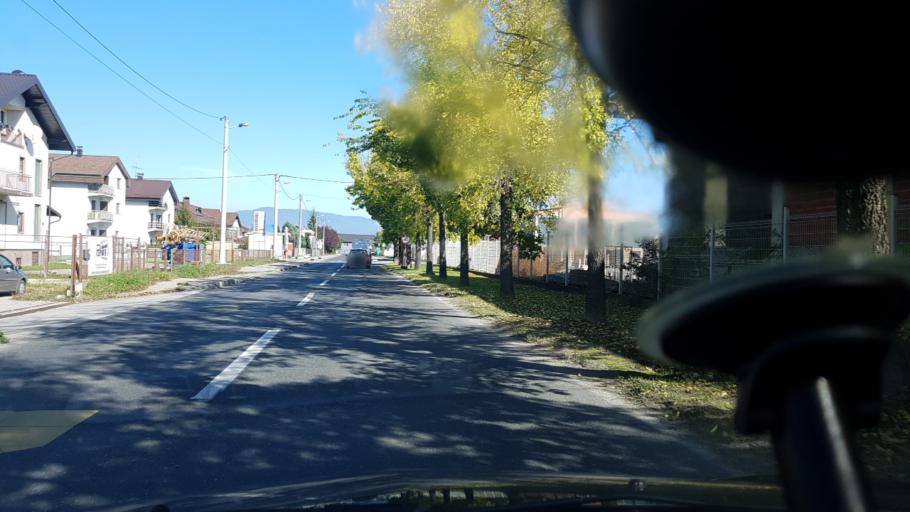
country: HR
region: Grad Zagreb
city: Lucko
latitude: 45.7574
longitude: 15.8922
